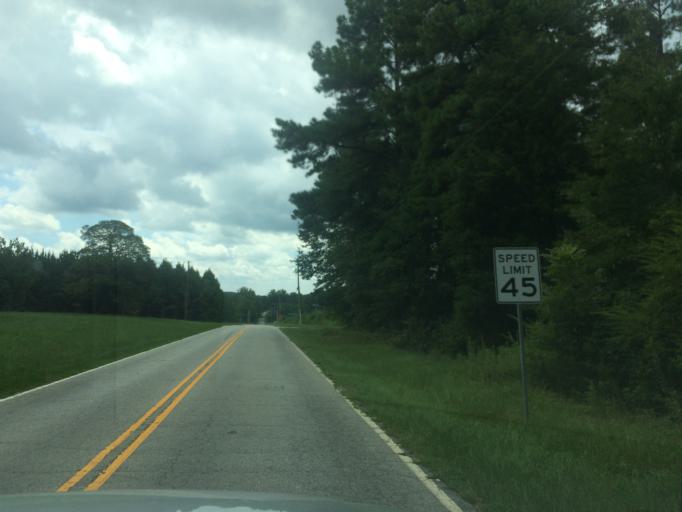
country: US
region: South Carolina
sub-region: Spartanburg County
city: Inman
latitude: 35.1524
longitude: -82.0362
